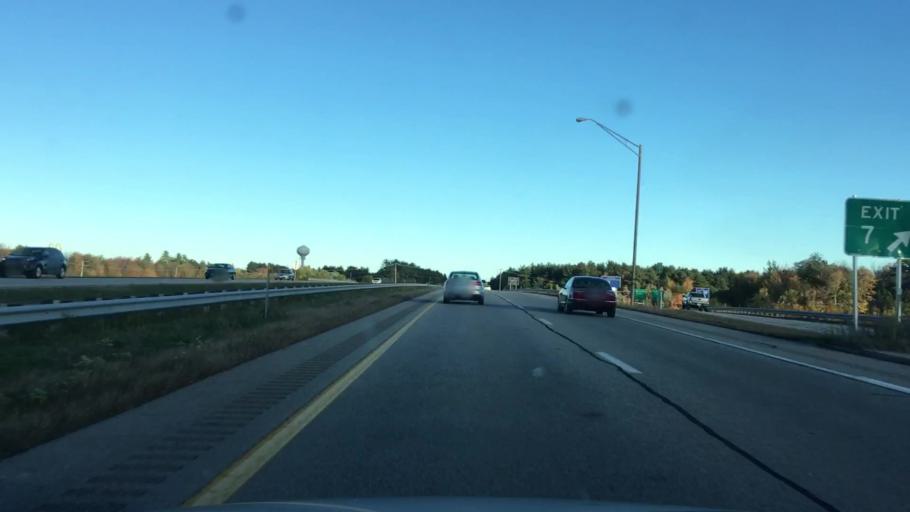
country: US
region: New Hampshire
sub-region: Rockingham County
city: Epping
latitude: 43.0272
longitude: -71.0779
